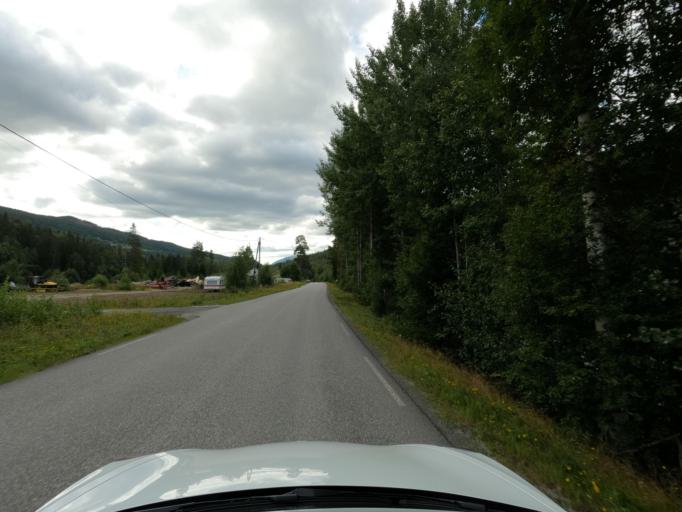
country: NO
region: Buskerud
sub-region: Nore og Uvdal
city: Rodberg
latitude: 60.0332
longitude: 8.8234
